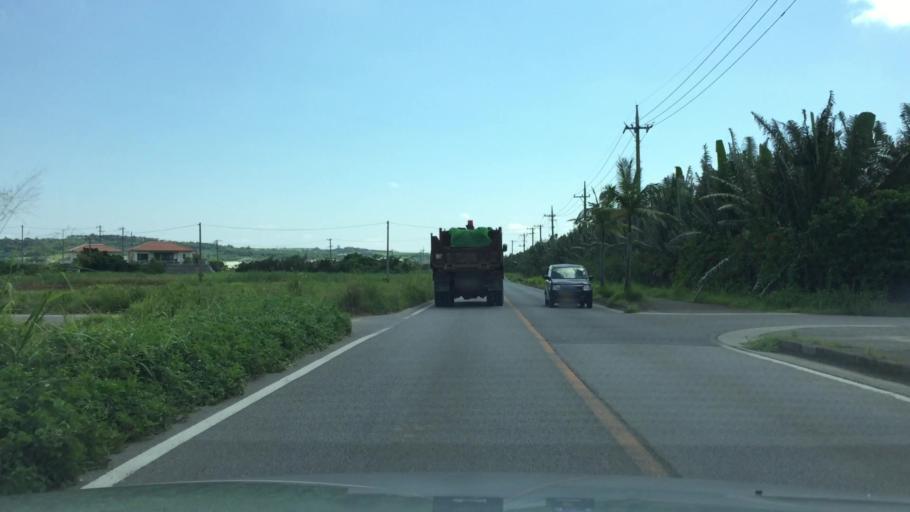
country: JP
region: Okinawa
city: Ishigaki
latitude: 24.3562
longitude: 124.1965
